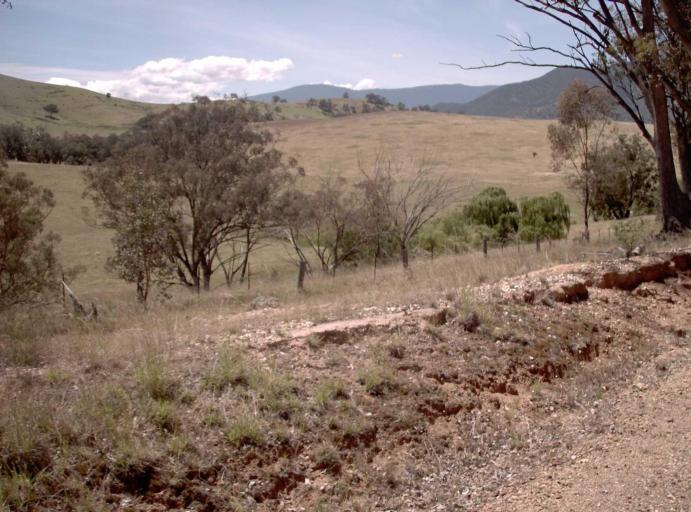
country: AU
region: Victoria
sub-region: East Gippsland
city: Bairnsdale
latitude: -37.1742
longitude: 147.6980
